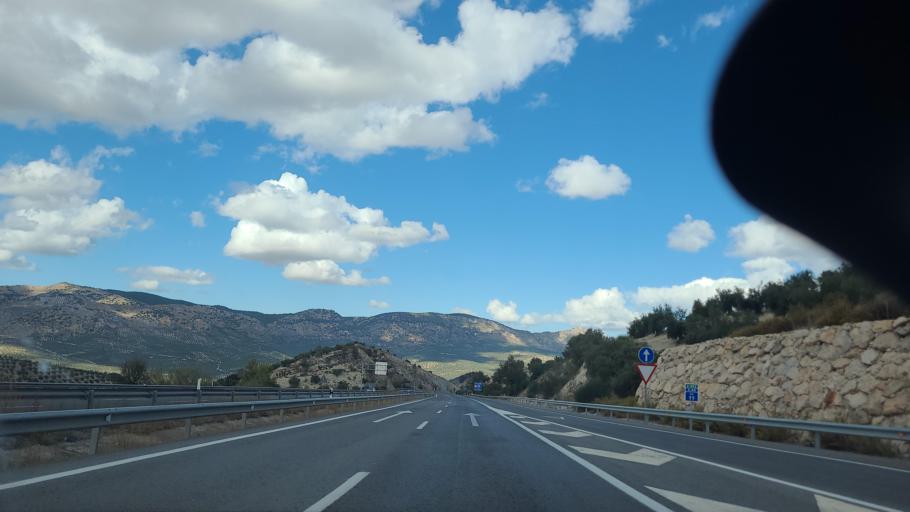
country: ES
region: Andalusia
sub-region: Provincia de Jaen
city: Campillo de Arenas
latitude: 37.5347
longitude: -3.6358
